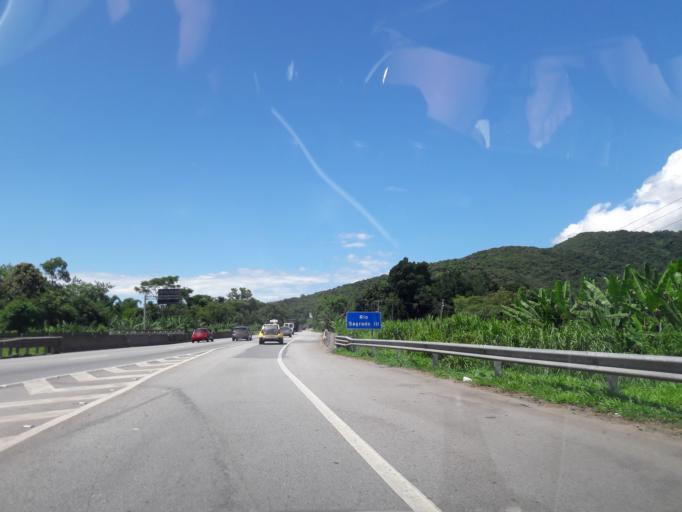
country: BR
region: Parana
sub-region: Antonina
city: Antonina
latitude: -25.5458
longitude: -48.7848
